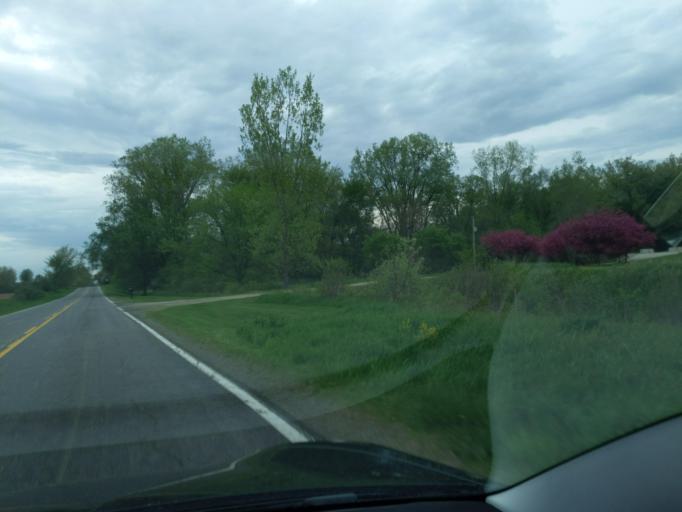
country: US
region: Michigan
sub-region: Ingham County
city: Stockbridge
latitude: 42.4457
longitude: -84.2584
